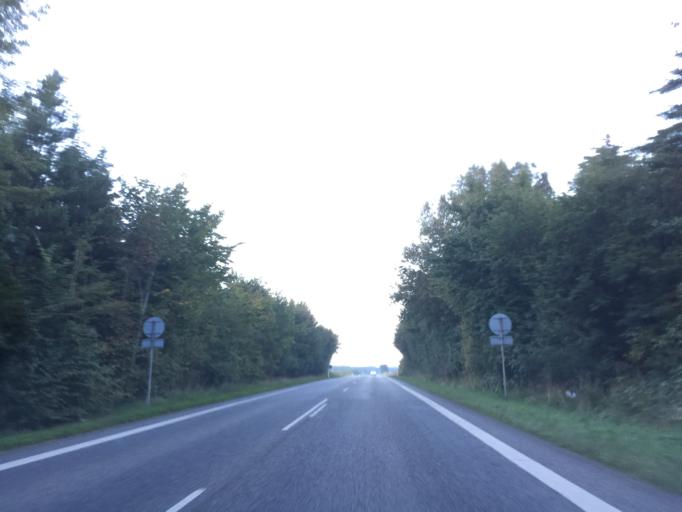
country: DK
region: South Denmark
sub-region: Aabenraa Kommune
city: Lojt Kirkeby
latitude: 55.0859
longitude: 9.4321
